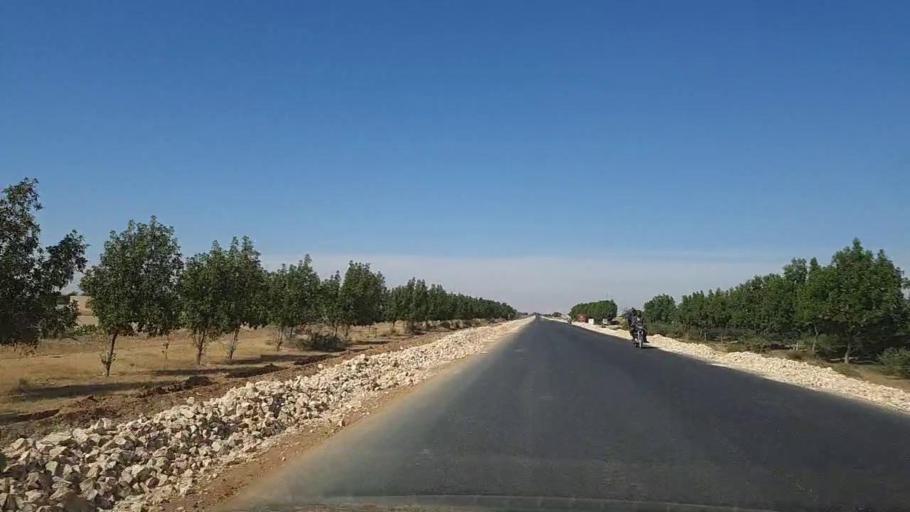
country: PK
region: Sindh
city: Kotri
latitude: 25.2722
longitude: 68.2165
